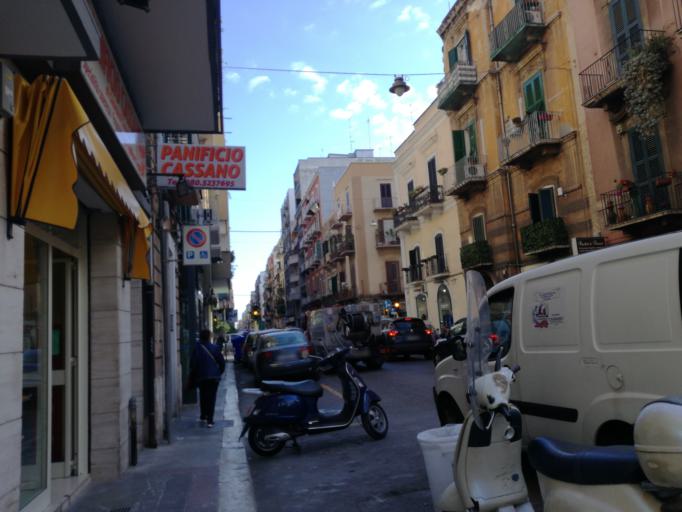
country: IT
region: Apulia
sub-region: Provincia di Bari
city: Bari
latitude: 41.1215
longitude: 16.8606
